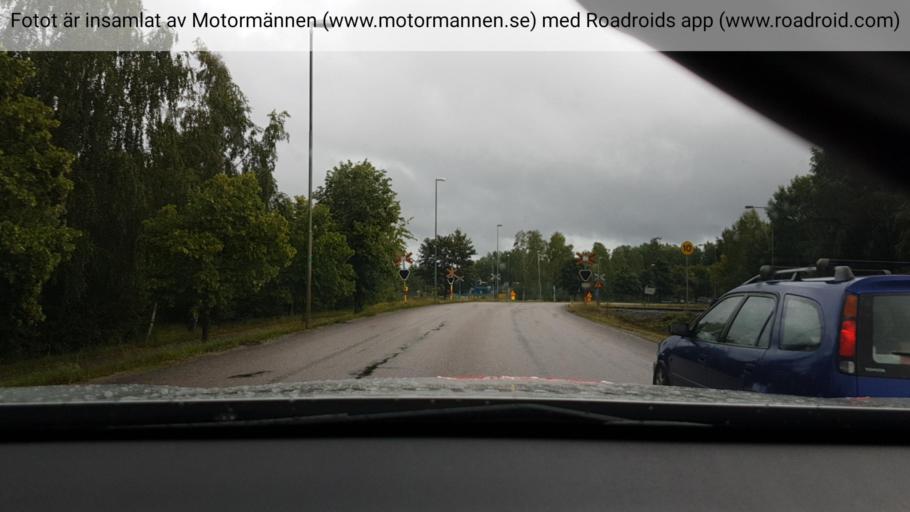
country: SE
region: Stockholm
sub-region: Haninge Kommun
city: Jordbro
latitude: 59.1484
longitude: 18.1231
